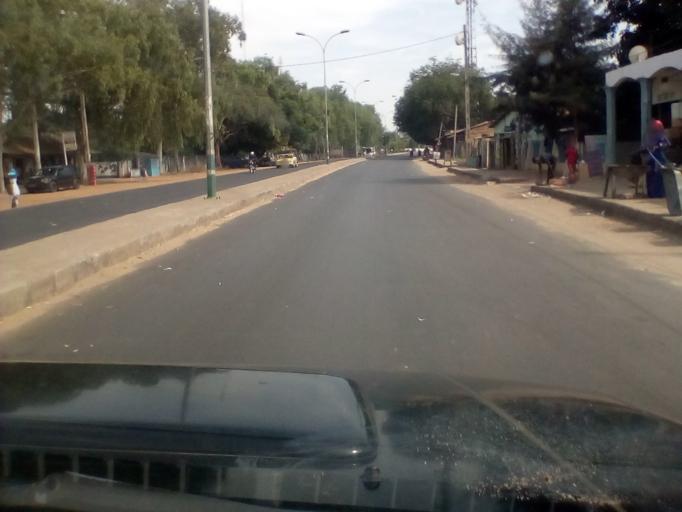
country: GM
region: Western
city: Abuko
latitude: 13.4021
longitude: -16.6569
